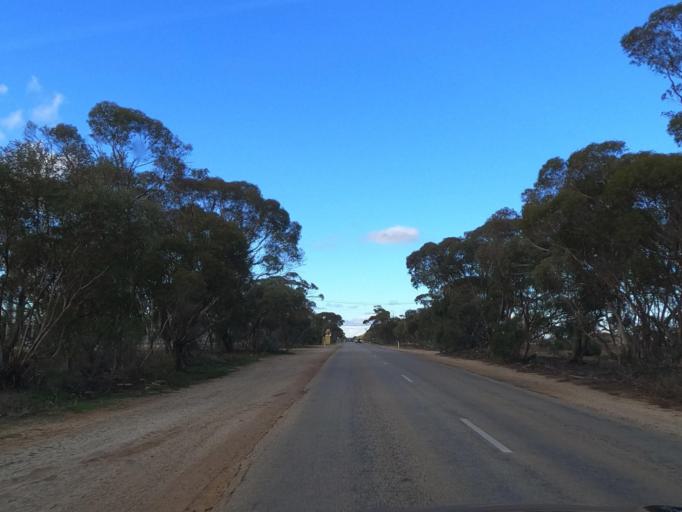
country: AU
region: Victoria
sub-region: Swan Hill
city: Swan Hill
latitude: -35.3466
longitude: 143.5208
